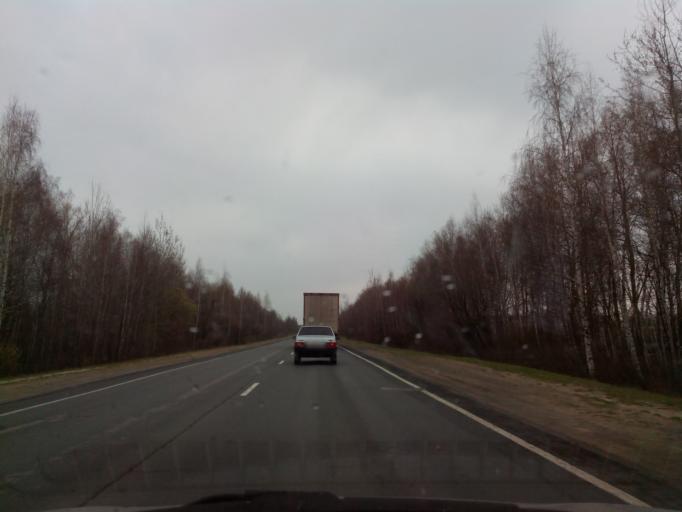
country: RU
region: Tambov
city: Pervomayskiy
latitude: 53.1060
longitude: 40.3936
